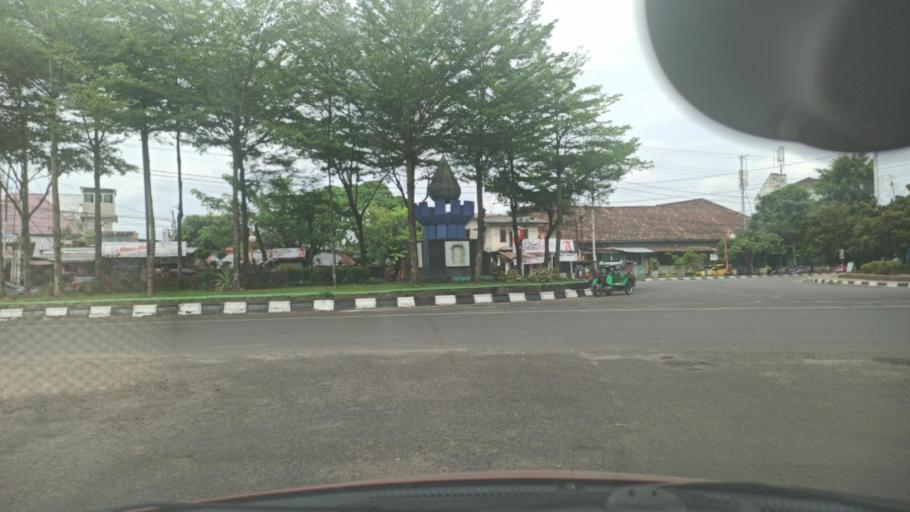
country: ID
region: South Sumatra
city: Plaju
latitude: -2.9881
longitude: 104.7470
